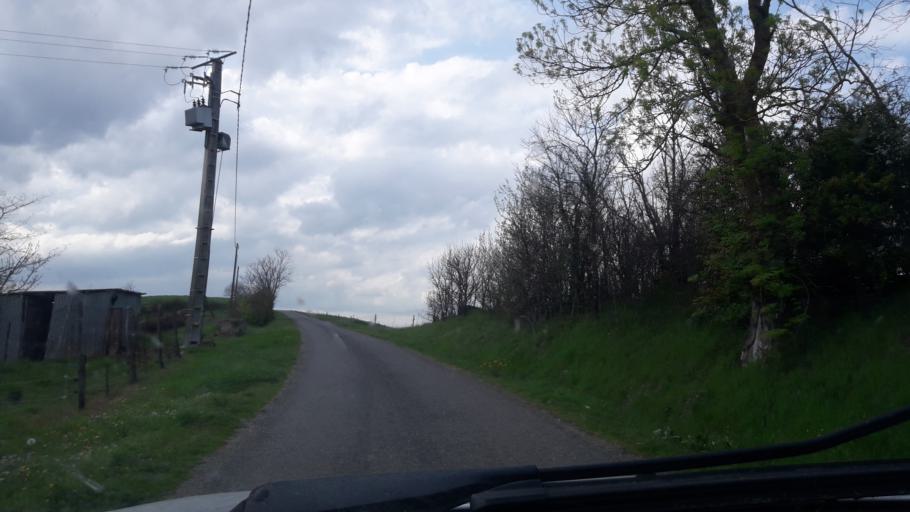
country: FR
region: Midi-Pyrenees
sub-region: Departement de l'Ariege
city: Lezat-sur-Leze
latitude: 43.1937
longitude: 1.3265
